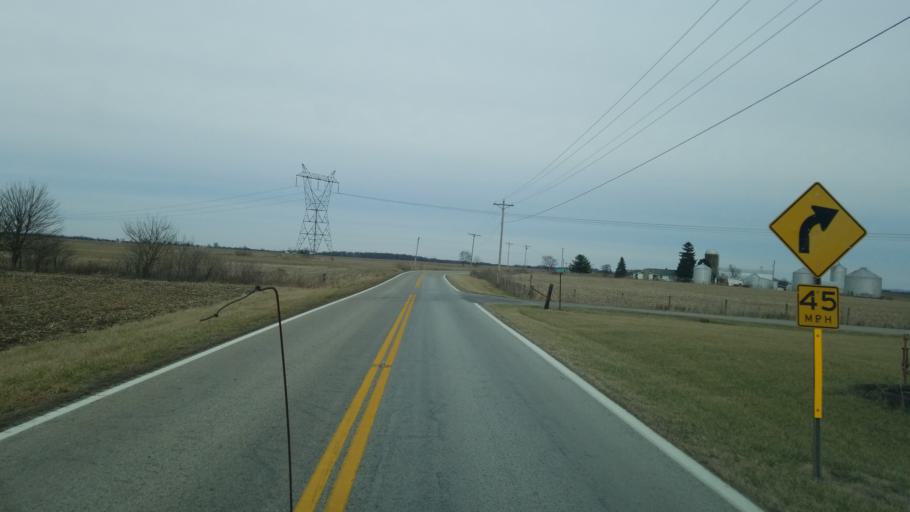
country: US
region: Ohio
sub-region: Pickaway County
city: Williamsport
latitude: 39.5226
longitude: -83.1332
